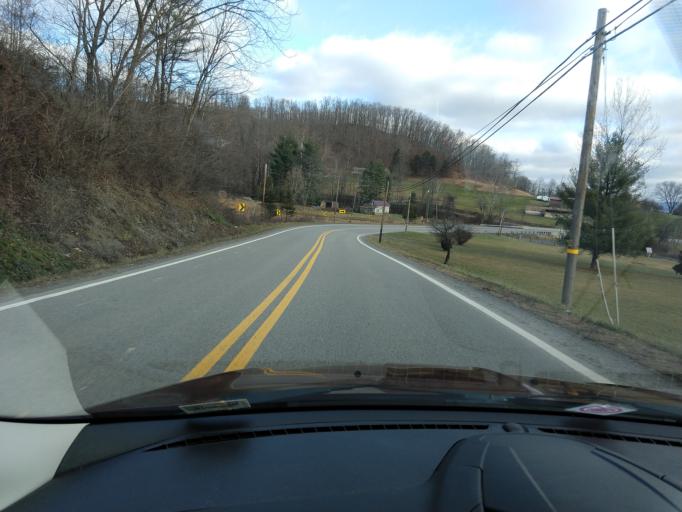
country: US
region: West Virginia
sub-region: Randolph County
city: Elkins
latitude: 38.7821
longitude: -79.9115
